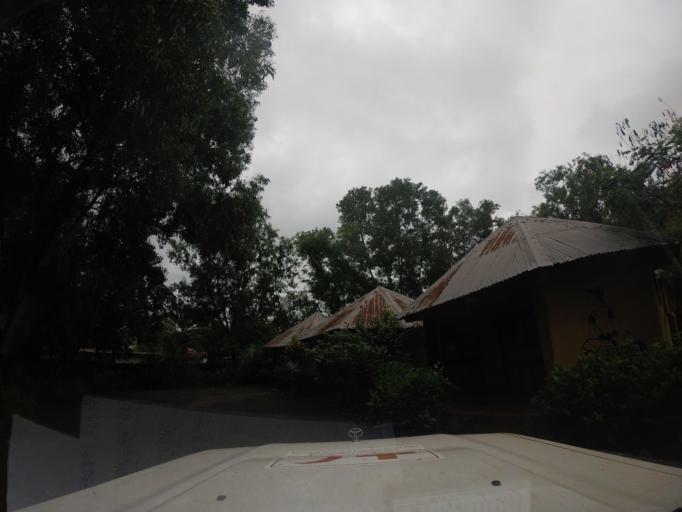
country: SL
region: Northern Province
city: Kambia
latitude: 9.1052
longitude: -12.9224
